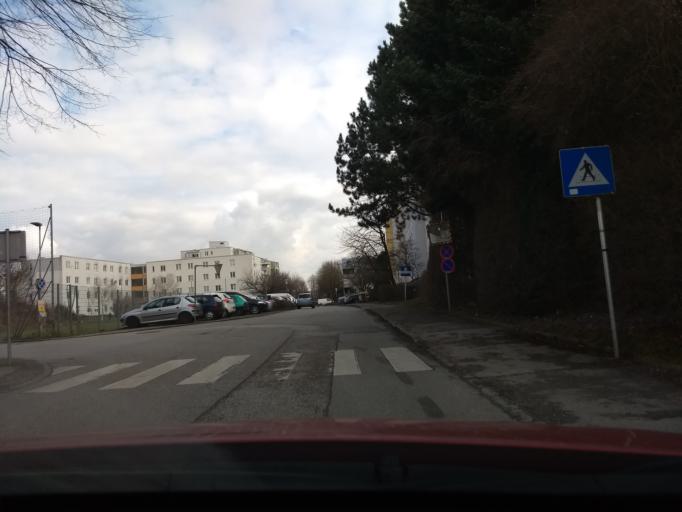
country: AT
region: Upper Austria
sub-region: Steyr Stadt
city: Steyr
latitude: 48.0625
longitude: 14.4238
